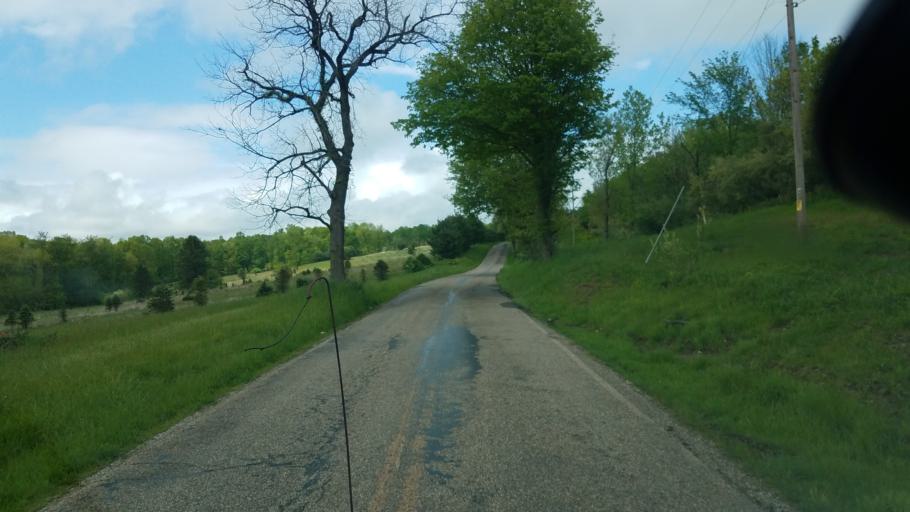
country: US
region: Ohio
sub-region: Tuscarawas County
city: Strasburg
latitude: 40.6222
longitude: -81.4200
